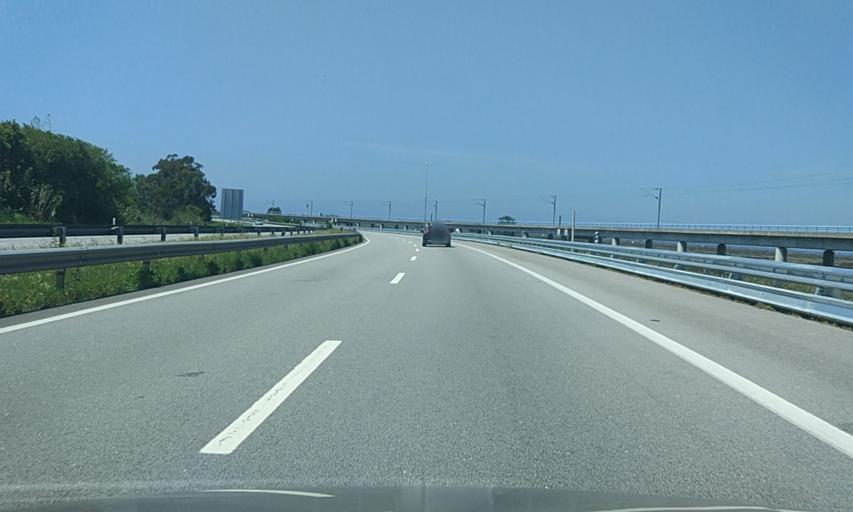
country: PT
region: Aveiro
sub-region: Aveiro
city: Aveiro
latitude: 40.6540
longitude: -8.6334
